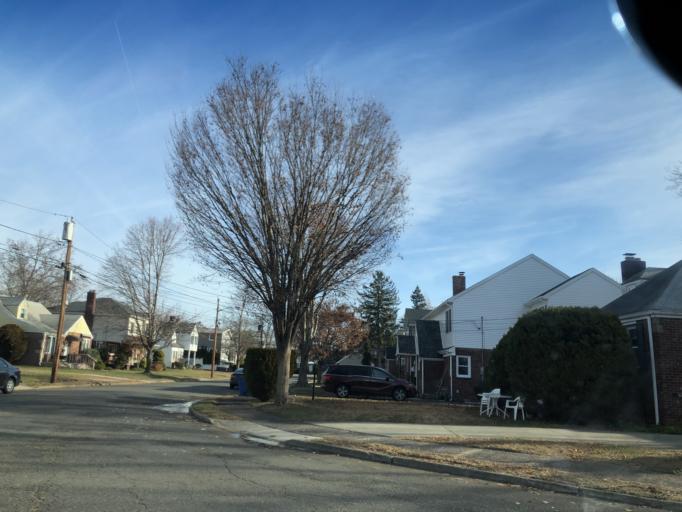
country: US
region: New Jersey
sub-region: Bergen County
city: Fair Lawn
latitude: 40.9310
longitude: -74.1283
